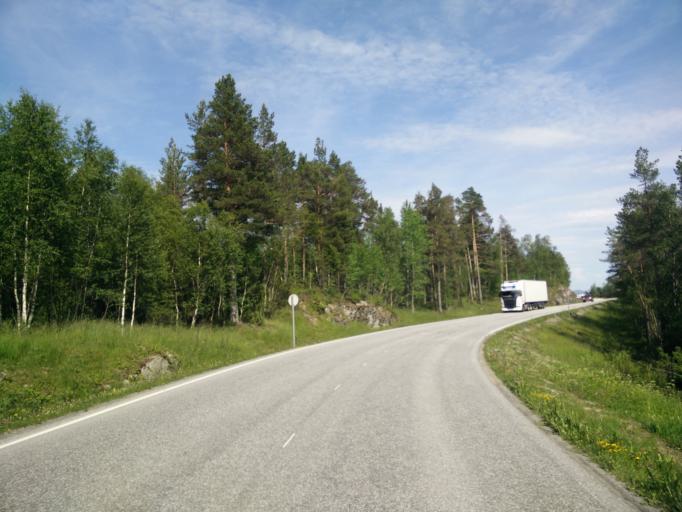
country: NO
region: More og Romsdal
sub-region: Tingvoll
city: Tingvoll
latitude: 63.0349
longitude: 8.0335
